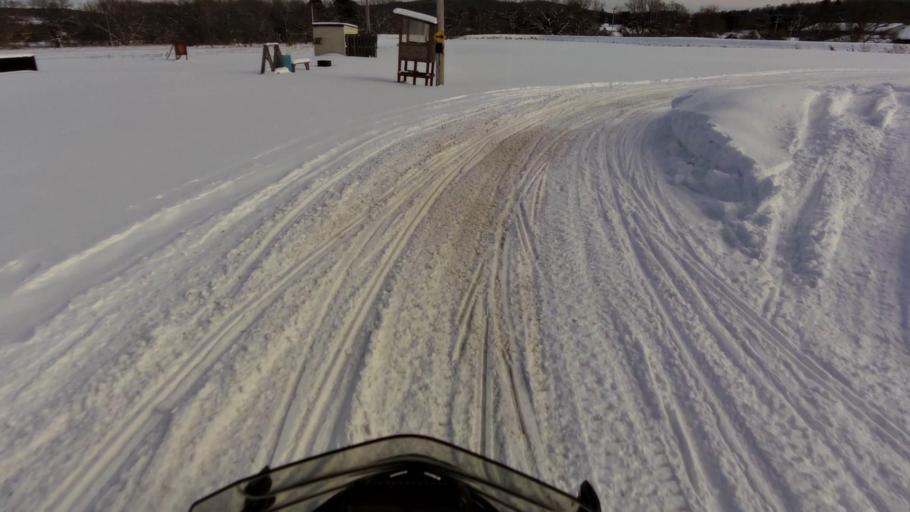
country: US
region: New York
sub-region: Cattaraugus County
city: Franklinville
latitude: 42.3388
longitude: -78.4668
